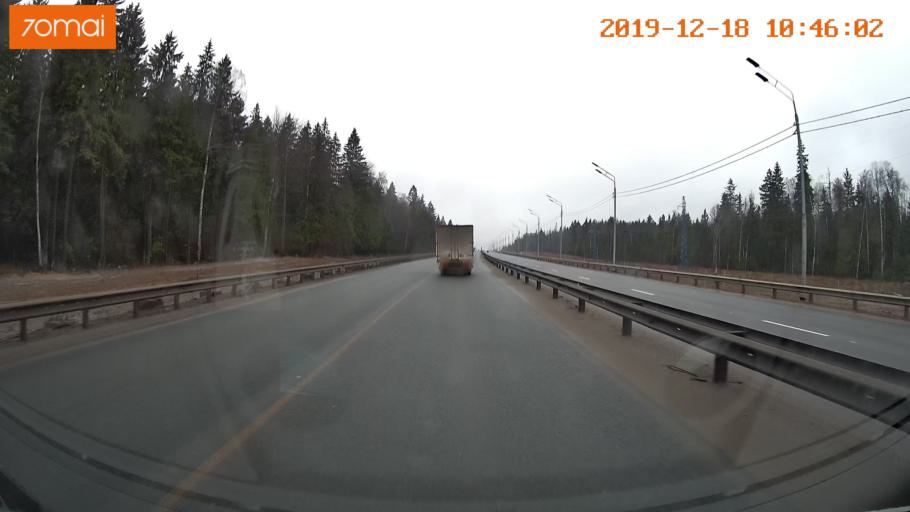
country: RU
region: Moskovskaya
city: Aprelevka
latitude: 55.4814
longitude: 37.0530
